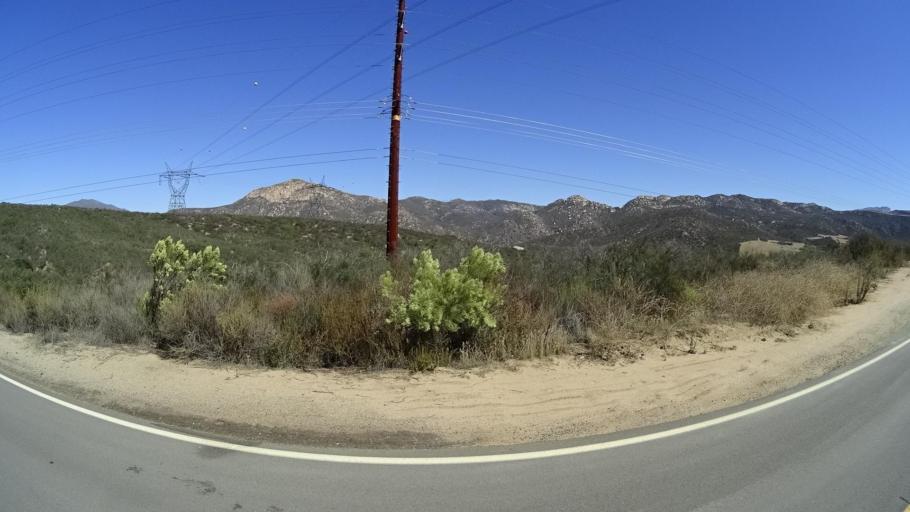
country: US
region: California
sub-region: San Diego County
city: Alpine
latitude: 32.7779
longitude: -116.7147
